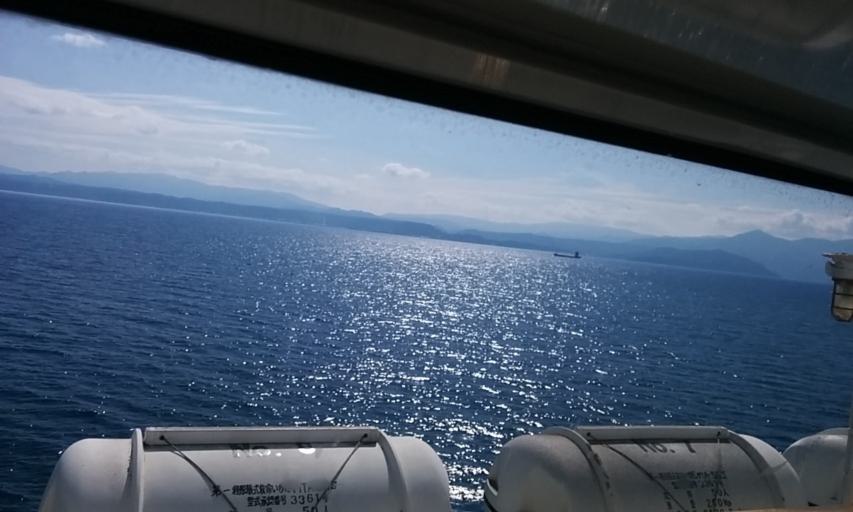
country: JP
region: Kagoshima
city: Ibusuki
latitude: 31.2744
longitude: 130.7018
